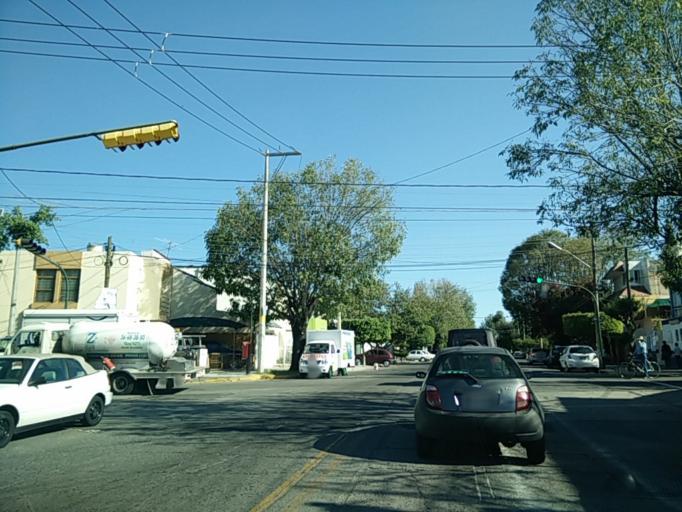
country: MX
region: Jalisco
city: Tlaquepaque
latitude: 20.6535
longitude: -103.3333
